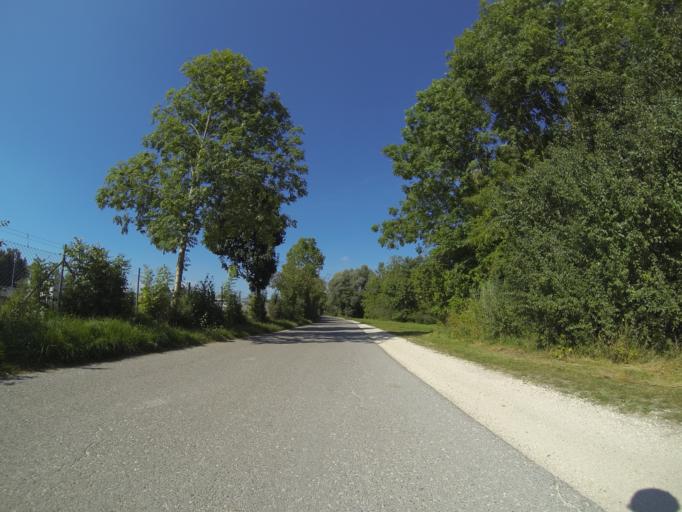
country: DE
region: Baden-Wuerttemberg
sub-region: Tuebingen Region
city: Erbach
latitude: 48.3254
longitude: 9.9077
